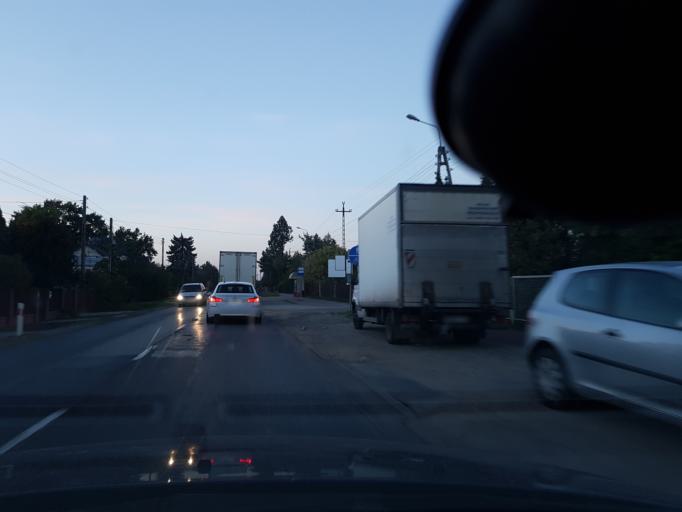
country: PL
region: Masovian Voivodeship
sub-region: Powiat grodziski
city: Grodzisk Mazowiecki
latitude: 52.0843
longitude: 20.6116
